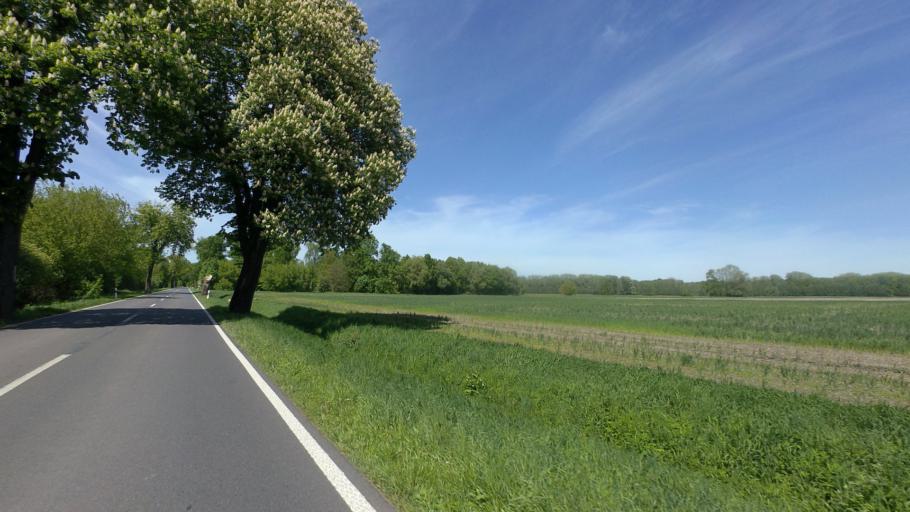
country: DE
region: Brandenburg
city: Baruth
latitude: 52.0794
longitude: 13.4528
